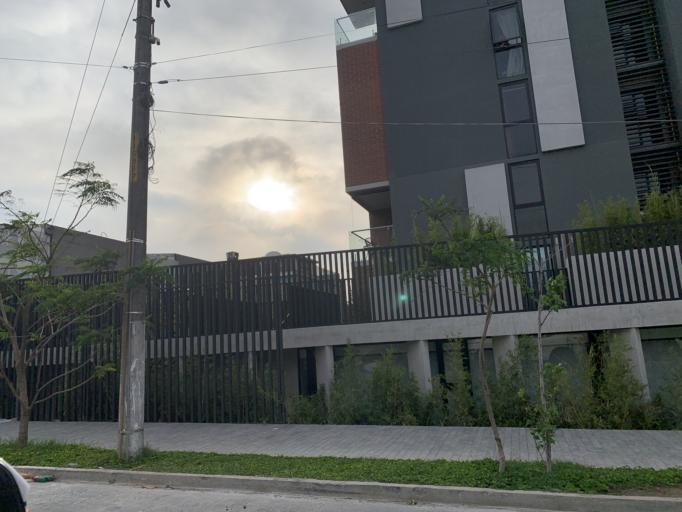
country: GT
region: Guatemala
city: Guatemala City
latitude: 14.6053
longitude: -90.5535
